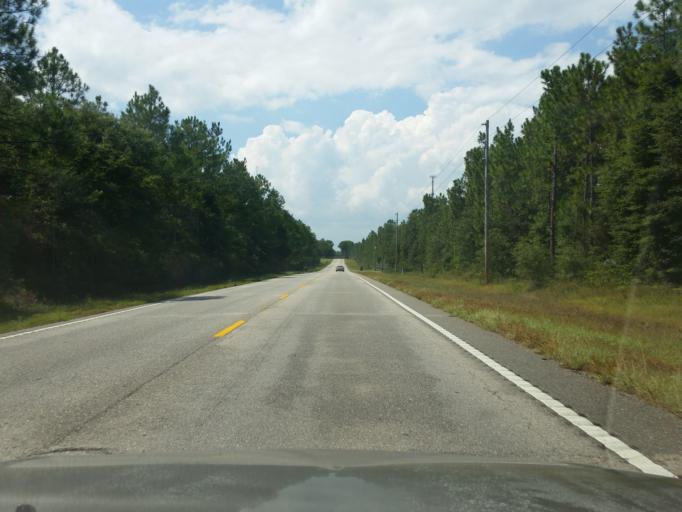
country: US
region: Alabama
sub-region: Baldwin County
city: Elberta
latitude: 30.5178
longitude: -87.4807
